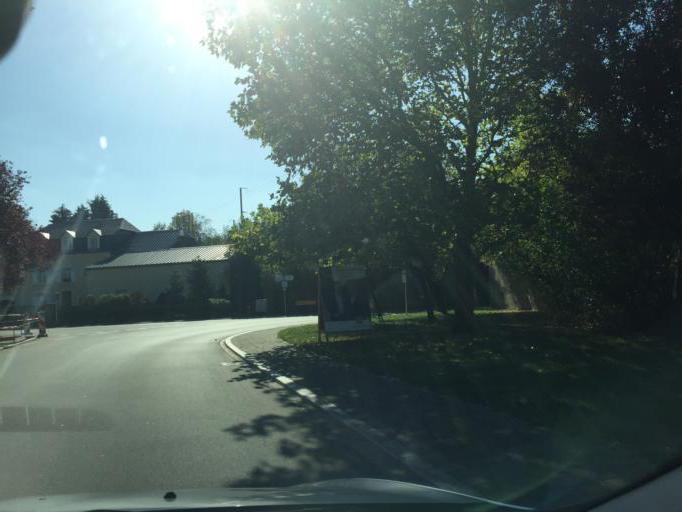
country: LU
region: Luxembourg
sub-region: Canton de Capellen
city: Mamer
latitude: 49.6235
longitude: 6.0233
